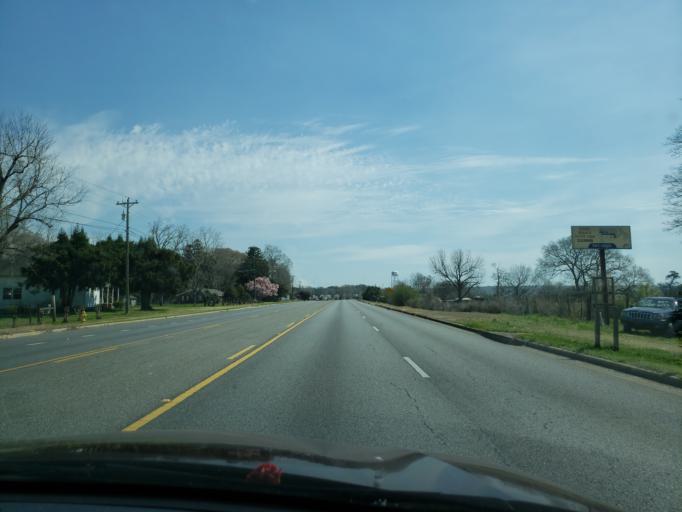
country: US
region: Alabama
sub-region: Elmore County
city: Wetumpka
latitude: 32.5373
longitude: -86.2608
